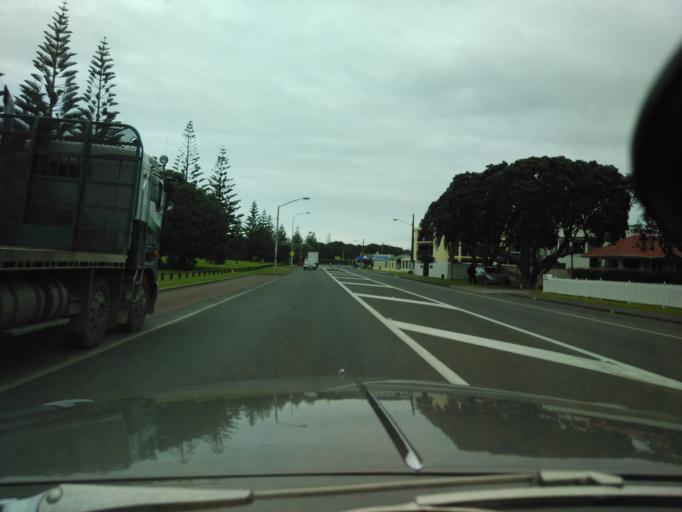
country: NZ
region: Auckland
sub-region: Auckland
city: Rothesay Bay
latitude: -36.5926
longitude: 174.6988
